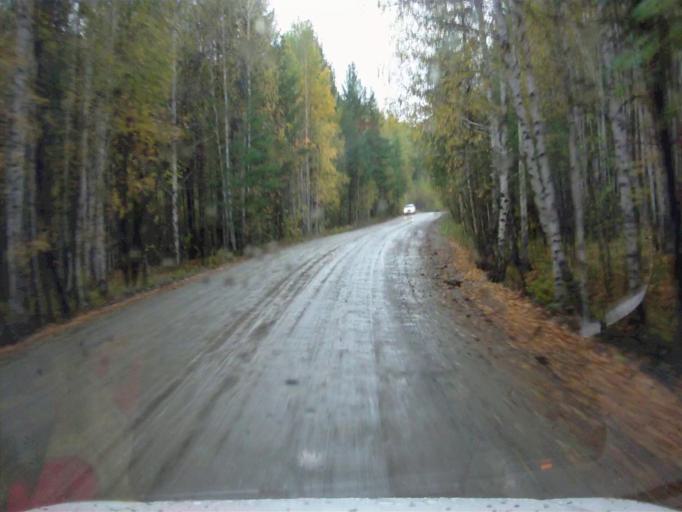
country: RU
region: Chelyabinsk
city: Kyshtym
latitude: 55.7493
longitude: 60.4881
